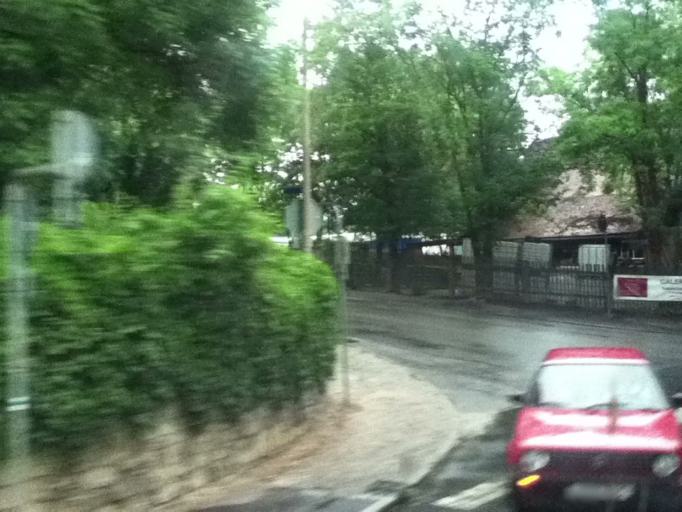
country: DE
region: Thuringia
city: Jena
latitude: 50.9305
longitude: 11.5829
